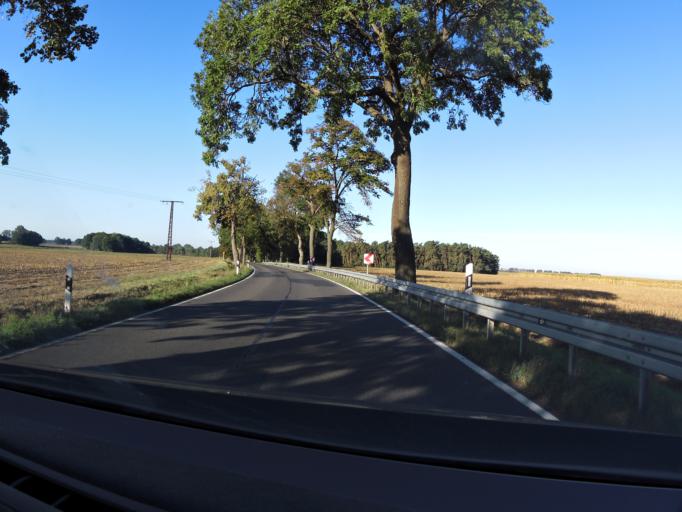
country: DE
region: Mecklenburg-Vorpommern
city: Alt-Sanitz
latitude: 53.8476
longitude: 13.6067
